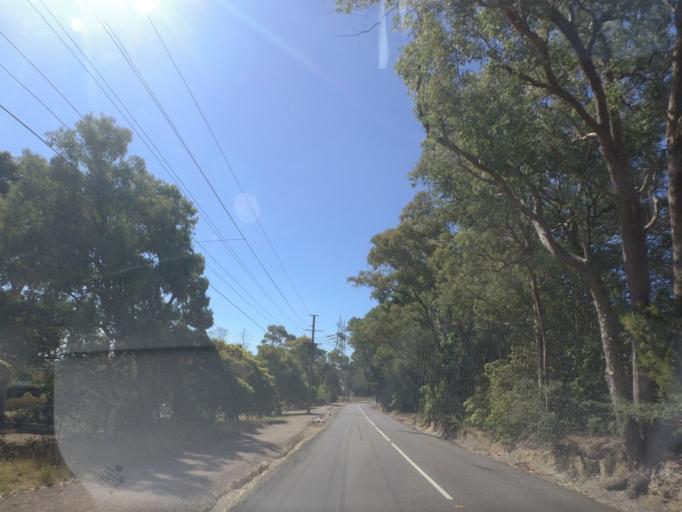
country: AU
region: Victoria
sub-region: Maroondah
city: Warranwood
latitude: -37.7677
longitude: 145.2502
